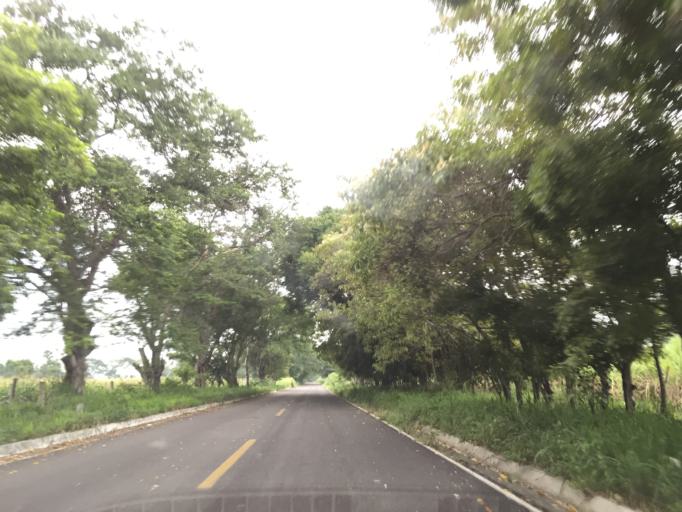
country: MX
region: Colima
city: Comala
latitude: 19.3797
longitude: -103.8029
